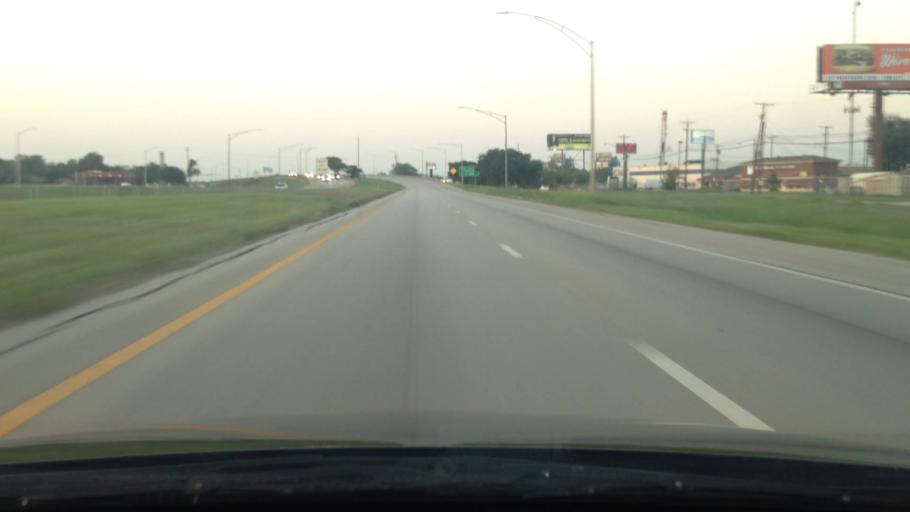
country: US
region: Texas
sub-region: Tarrant County
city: Forest Hill
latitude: 32.7161
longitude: -97.2269
